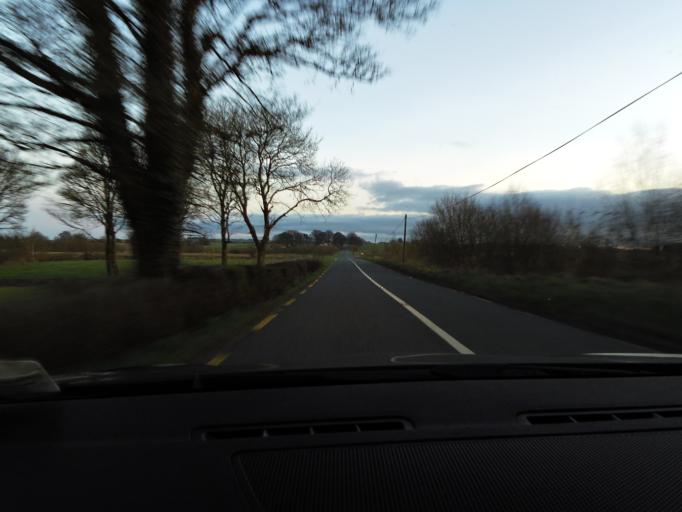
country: IE
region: Connaught
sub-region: Roscommon
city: Boyle
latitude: 53.8902
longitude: -8.2502
